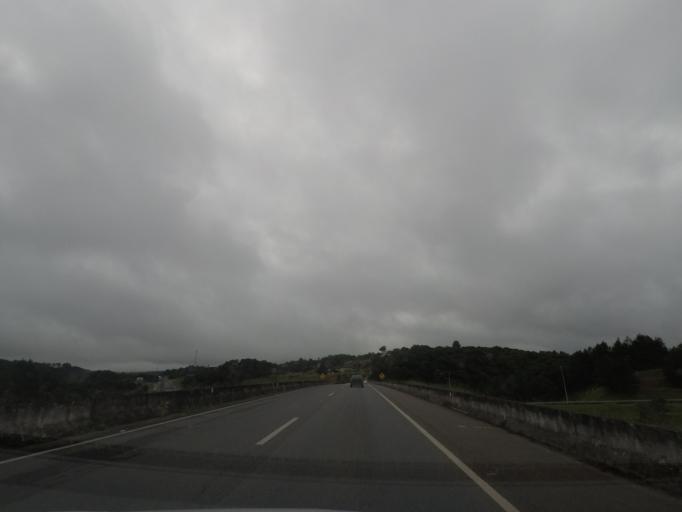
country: BR
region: Parana
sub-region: Quatro Barras
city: Quatro Barras
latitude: -25.3467
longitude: -49.0458
